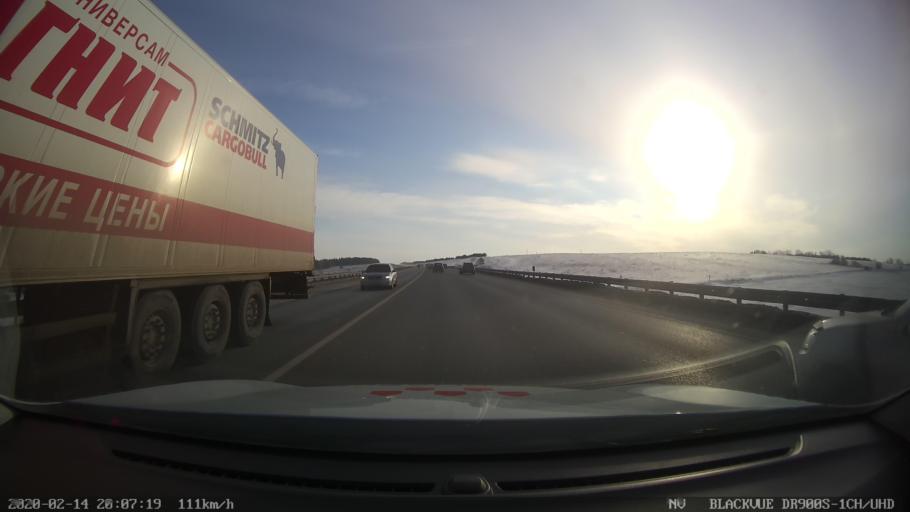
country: RU
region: Tatarstan
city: Verkhniy Uslon
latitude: 55.7231
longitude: 48.8353
